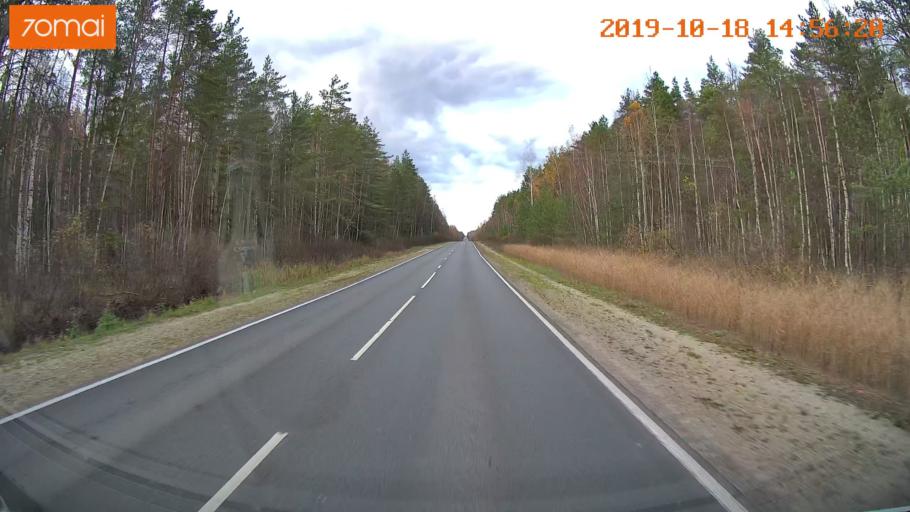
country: RU
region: Vladimir
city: Kurlovo
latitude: 55.4632
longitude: 40.5880
